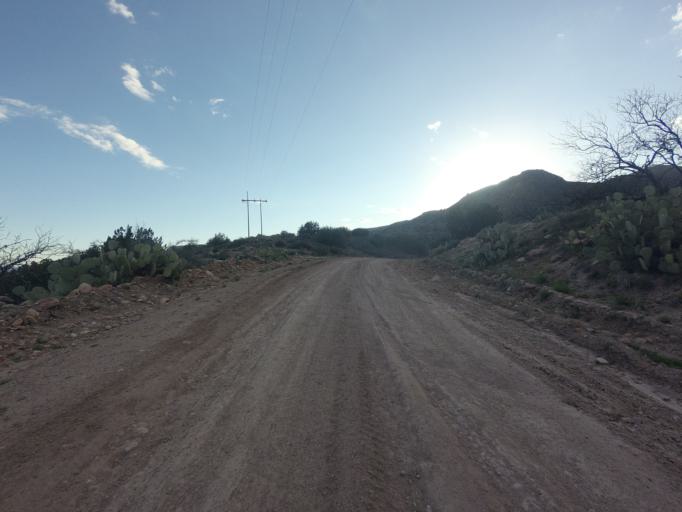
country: US
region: Arizona
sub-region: Gila County
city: Pine
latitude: 34.3712
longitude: -111.6648
